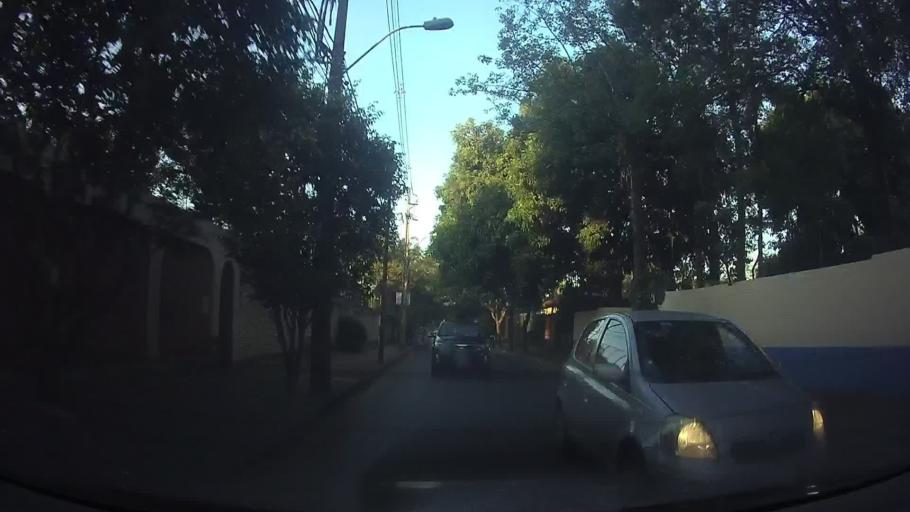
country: PY
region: Central
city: Lambare
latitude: -25.3022
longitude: -57.5752
